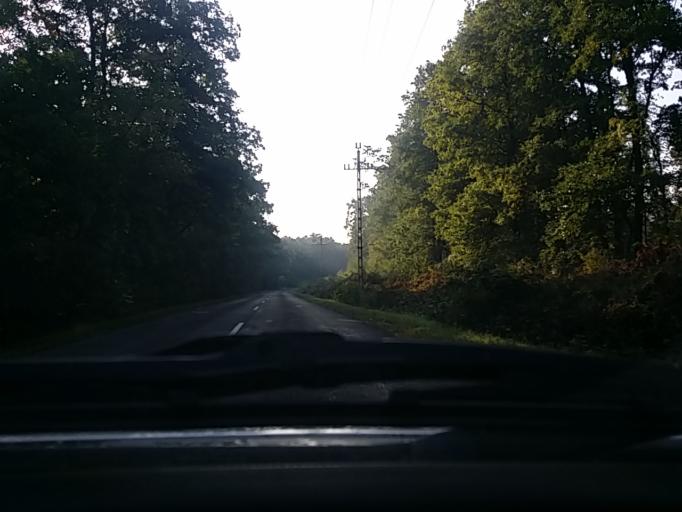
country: HU
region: Pest
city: Nagykovacsi
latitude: 47.7115
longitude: 19.0148
